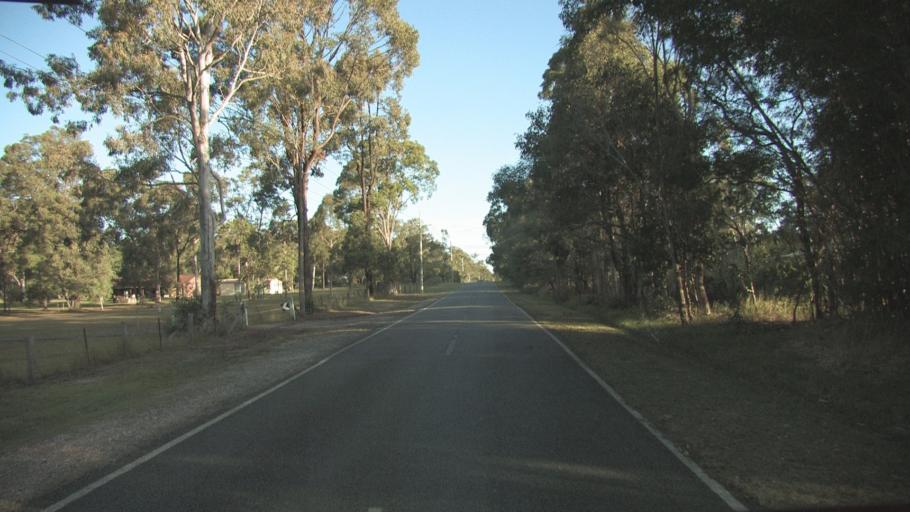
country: AU
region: Queensland
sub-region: Logan
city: Waterford West
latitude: -27.7247
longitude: 153.1414
